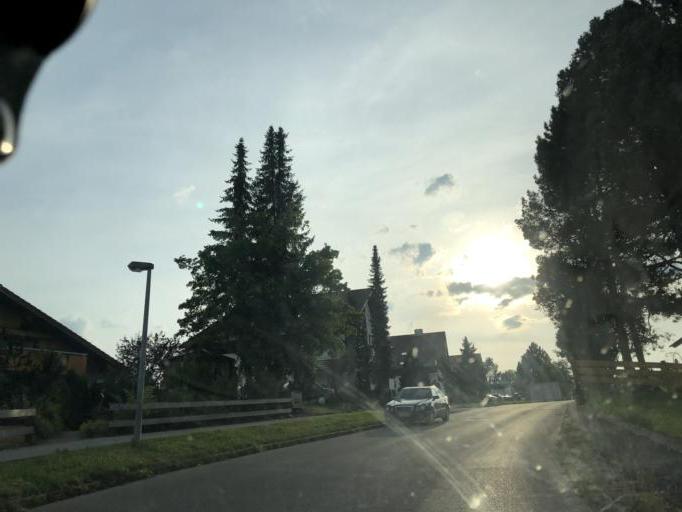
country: DE
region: Bavaria
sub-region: Swabia
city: Oy-Mittelberg
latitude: 47.6433
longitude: 10.4508
